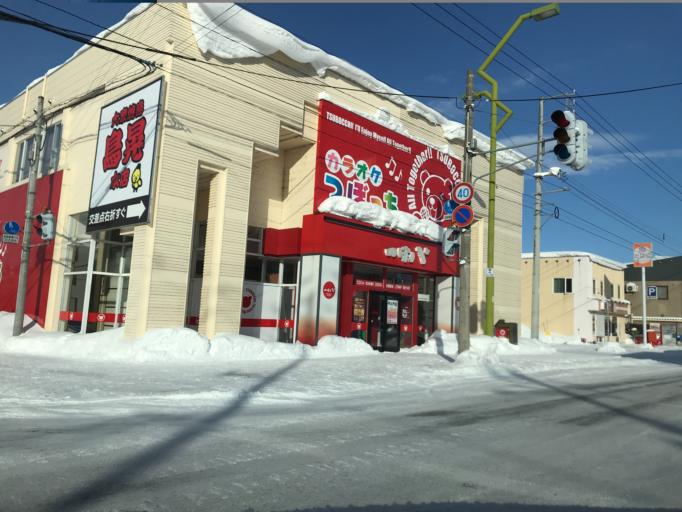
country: JP
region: Hokkaido
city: Nayoro
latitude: 44.3494
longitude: 142.4572
